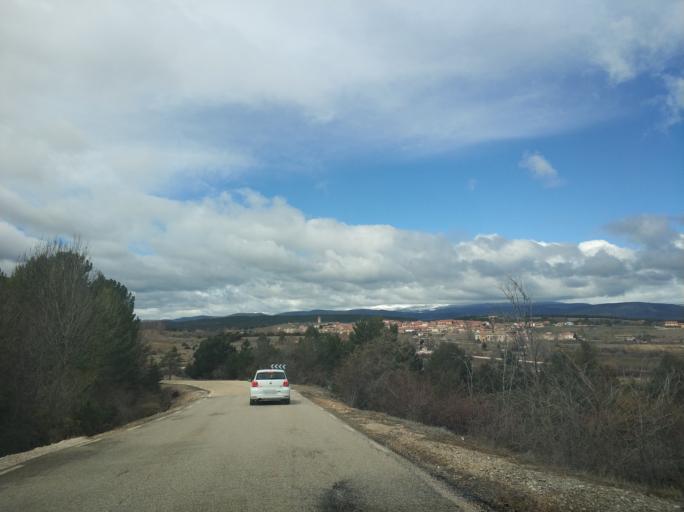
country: ES
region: Castille and Leon
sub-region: Provincia de Soria
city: Abejar
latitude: 41.7985
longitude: -2.7794
